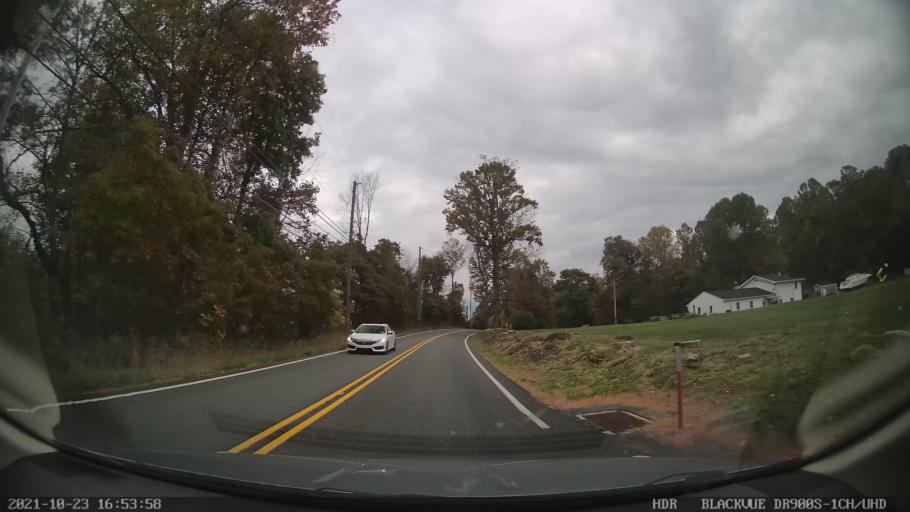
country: US
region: Pennsylvania
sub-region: Berks County
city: Red Lion
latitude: 40.4572
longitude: -75.5812
